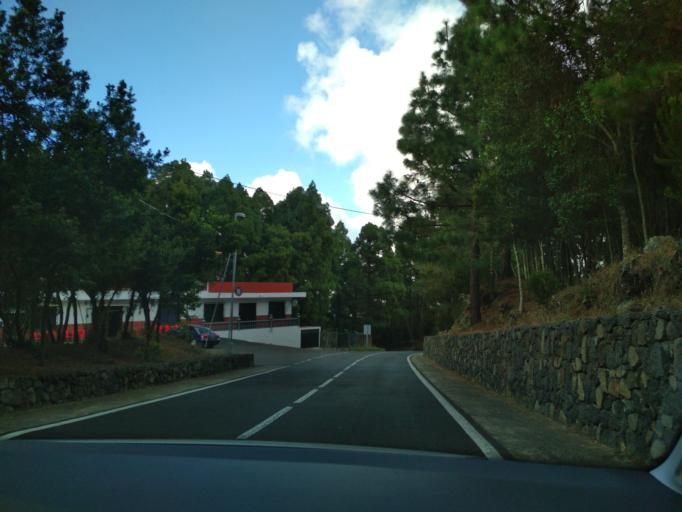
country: ES
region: Canary Islands
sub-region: Provincia de Santa Cruz de Tenerife
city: Garachico
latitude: 28.3408
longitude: -16.7553
